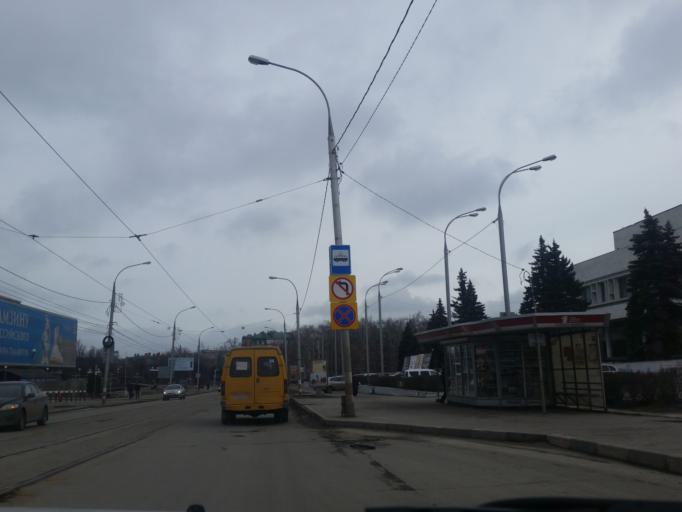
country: RU
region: Ulyanovsk
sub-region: Ulyanovskiy Rayon
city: Ulyanovsk
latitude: 54.3191
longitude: 48.4038
